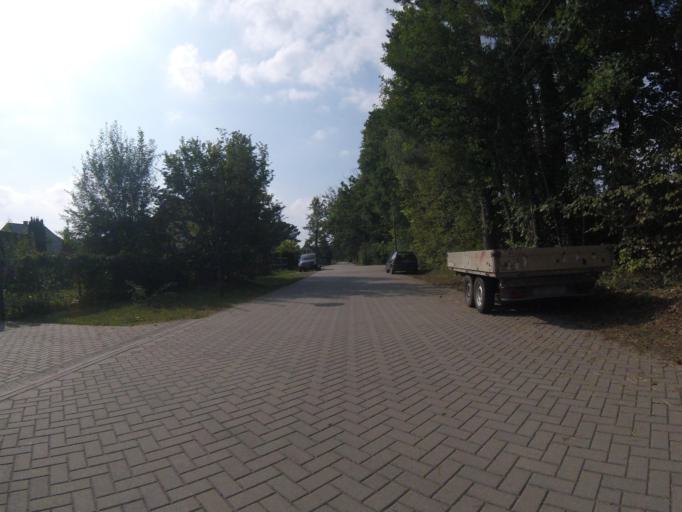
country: DE
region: Brandenburg
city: Bestensee
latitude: 52.2259
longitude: 13.6683
